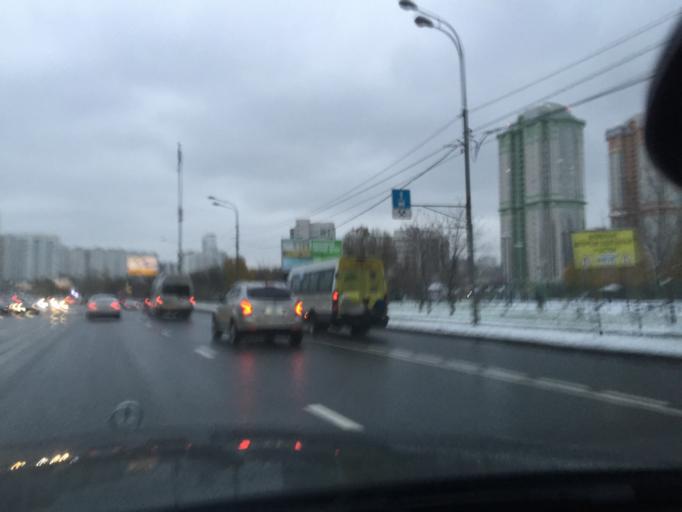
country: RU
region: Moscow
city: Troparevo
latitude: 55.6548
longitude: 37.4799
